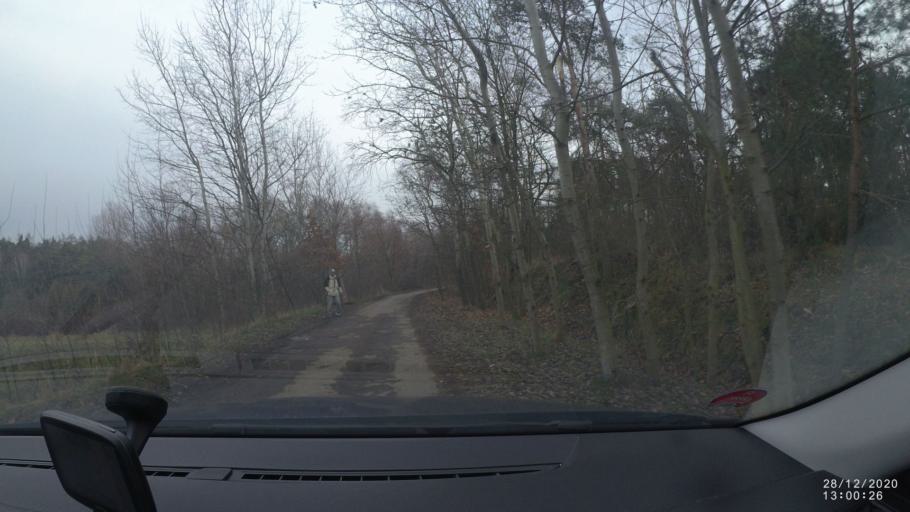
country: CZ
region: Praha
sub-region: Praha 20
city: Horni Pocernice
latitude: 50.1465
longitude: 14.6023
